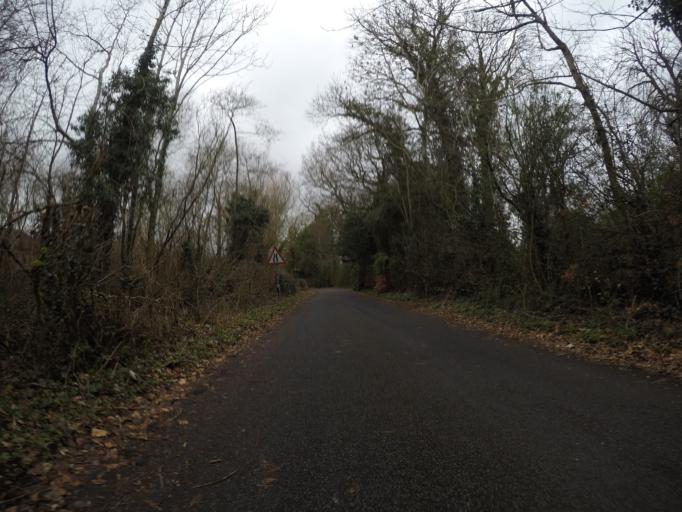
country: GB
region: Scotland
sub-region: North Ayrshire
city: Springside
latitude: 55.6297
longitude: -4.6184
